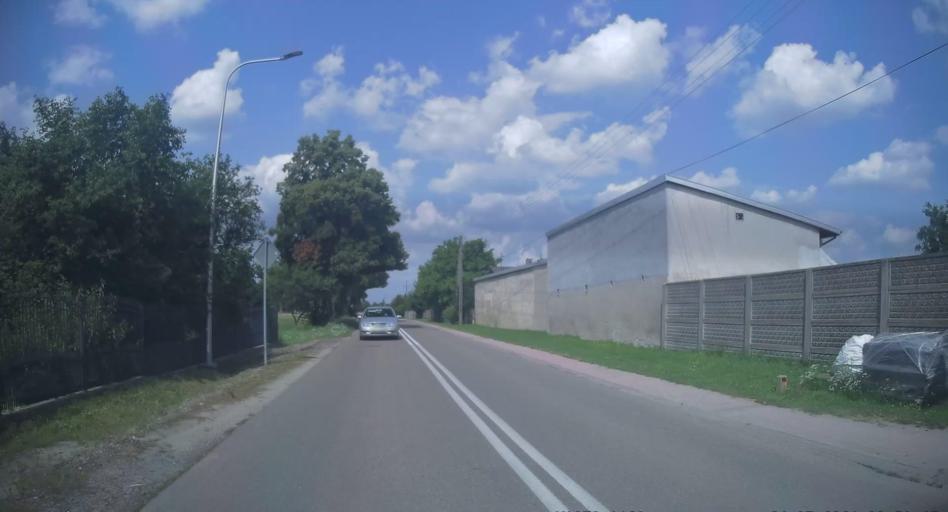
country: PL
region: Lodz Voivodeship
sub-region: Powiat tomaszowski
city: Lubochnia
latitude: 51.5672
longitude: 20.1123
